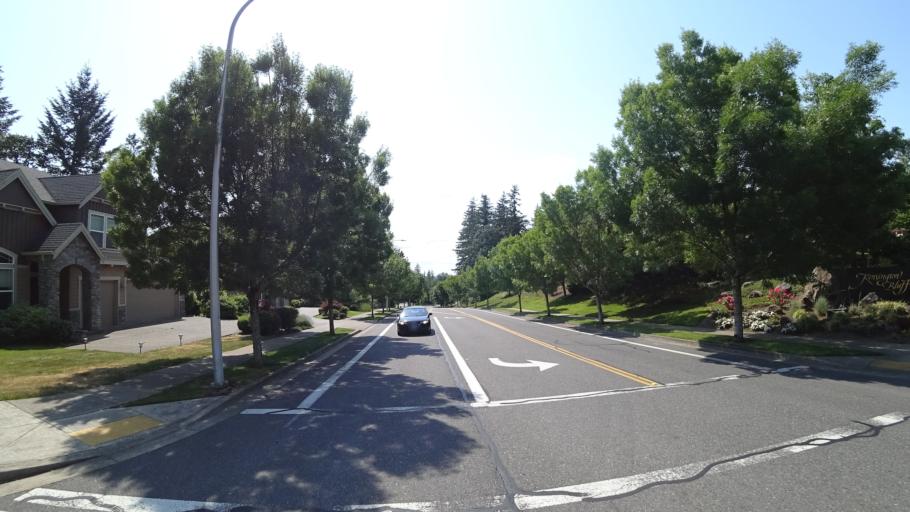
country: US
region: Oregon
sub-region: Clackamas County
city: Happy Valley
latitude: 45.4401
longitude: -122.5520
